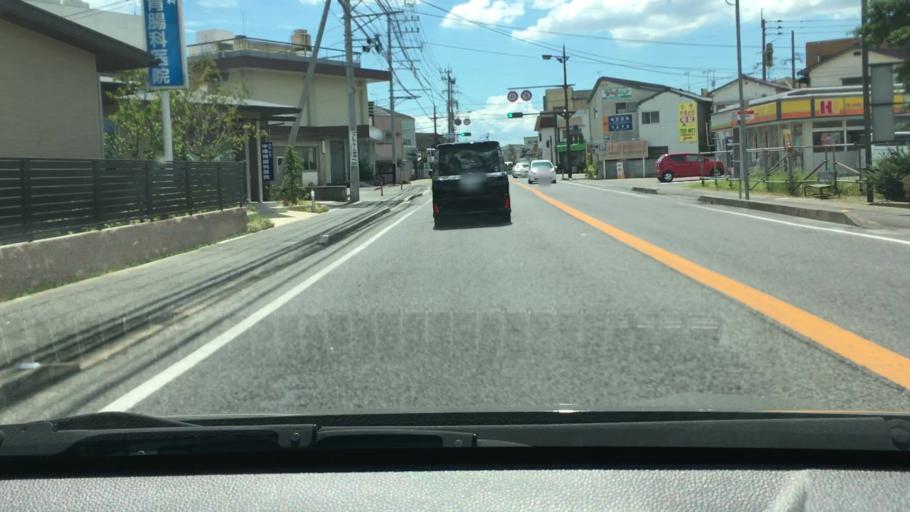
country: JP
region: Saga Prefecture
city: Kanzakimachi-kanzaki
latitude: 33.3138
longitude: 130.3759
